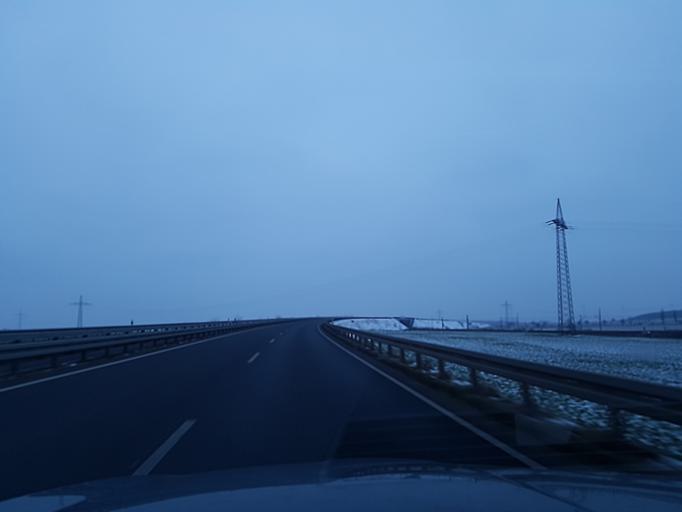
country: DE
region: Saxony
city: Riesa
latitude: 51.2910
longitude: 13.2765
